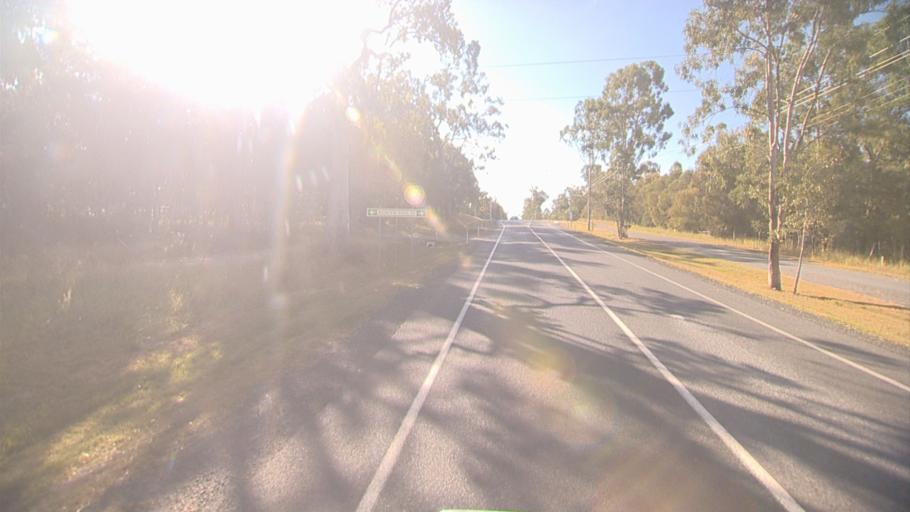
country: AU
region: Queensland
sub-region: Logan
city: North Maclean
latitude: -27.7920
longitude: 152.9814
